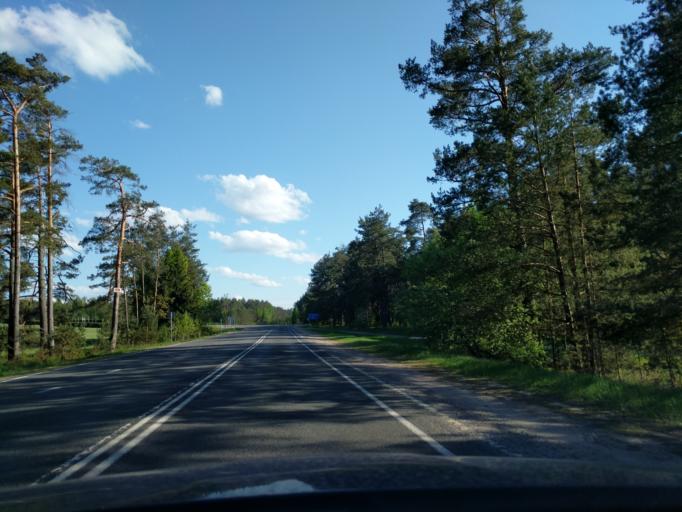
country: BY
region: Minsk
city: Myadzyel
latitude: 54.8301
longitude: 26.9412
